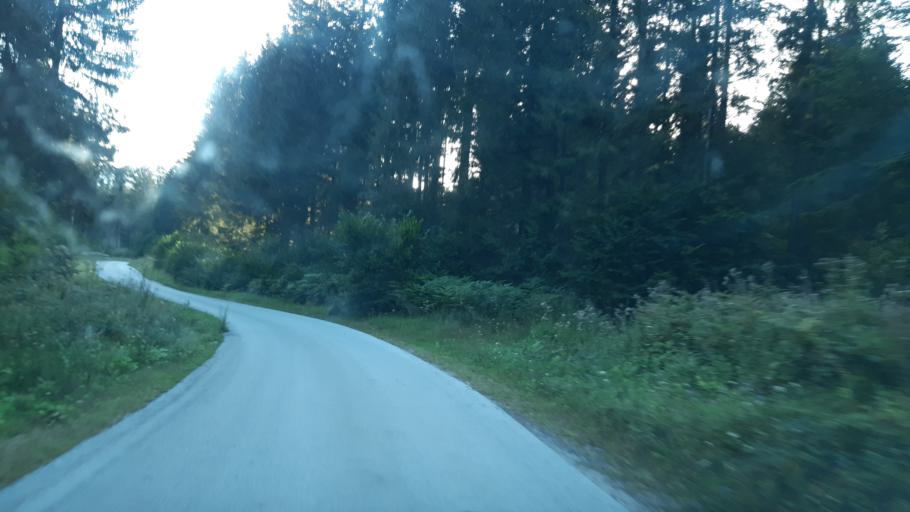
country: SI
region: Kocevje
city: Kocevje
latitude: 45.6589
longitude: 14.8977
